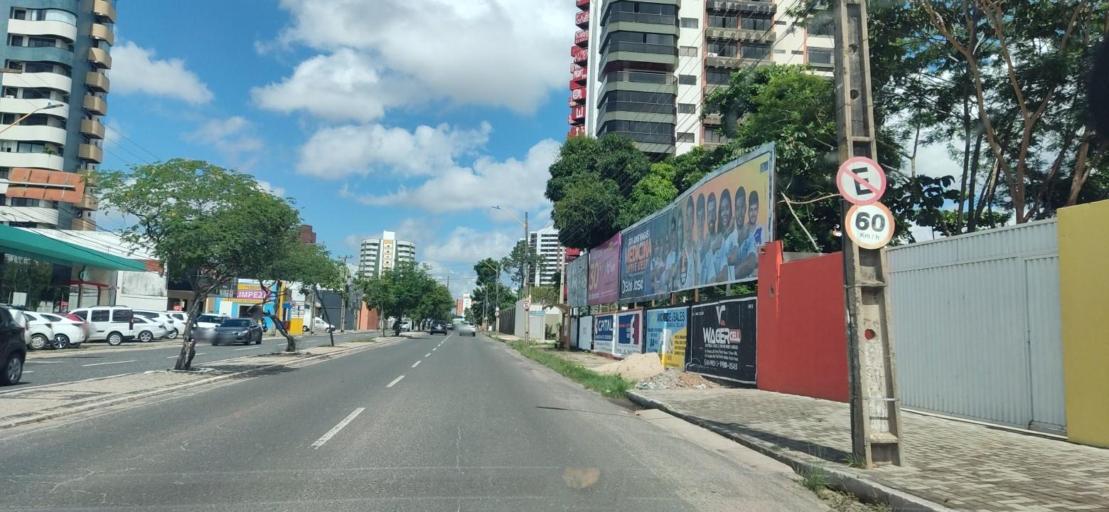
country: BR
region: Piaui
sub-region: Teresina
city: Teresina
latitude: -5.0703
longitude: -42.7729
